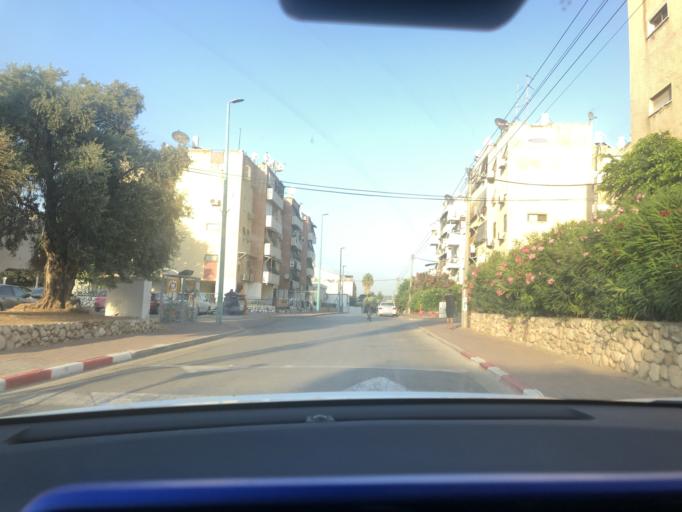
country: IL
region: Central District
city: Lod
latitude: 31.9535
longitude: 34.9015
